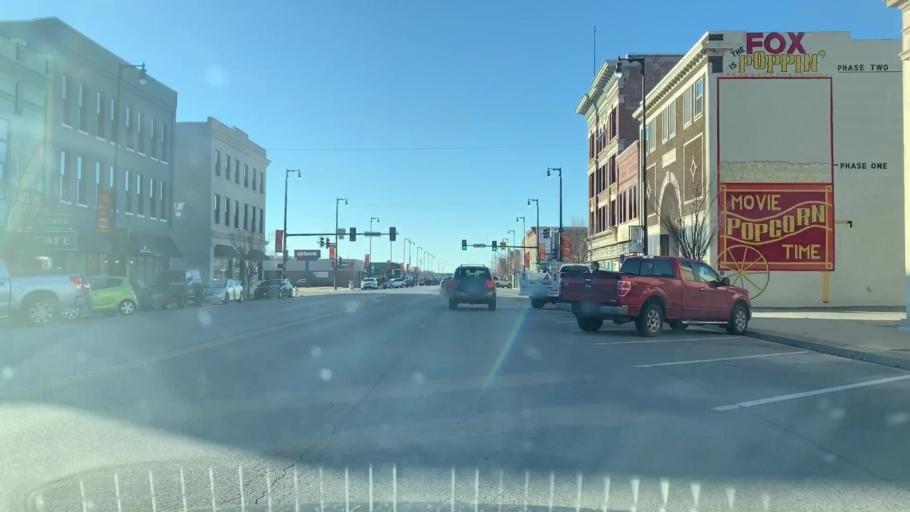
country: US
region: Kansas
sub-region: Crawford County
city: Pittsburg
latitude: 37.4118
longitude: -94.7049
